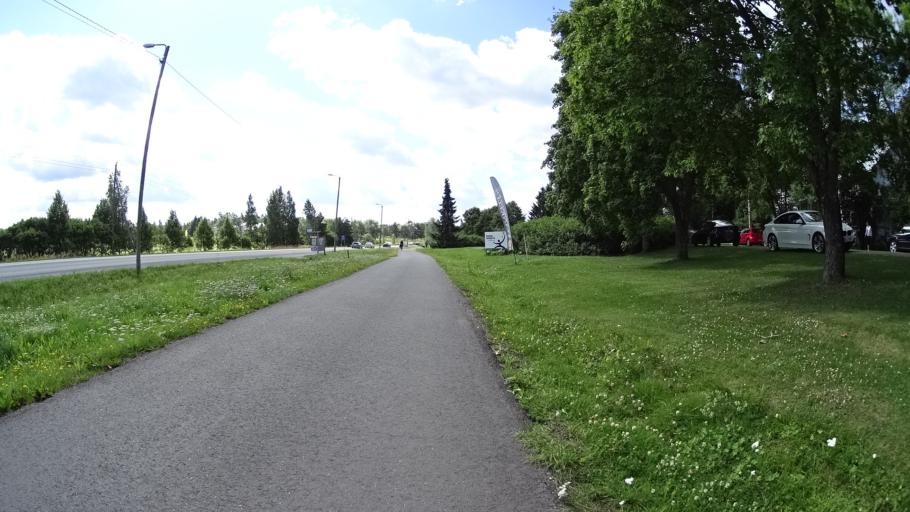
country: FI
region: Uusimaa
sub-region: Helsinki
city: Tuusula
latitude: 60.4183
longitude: 25.0525
